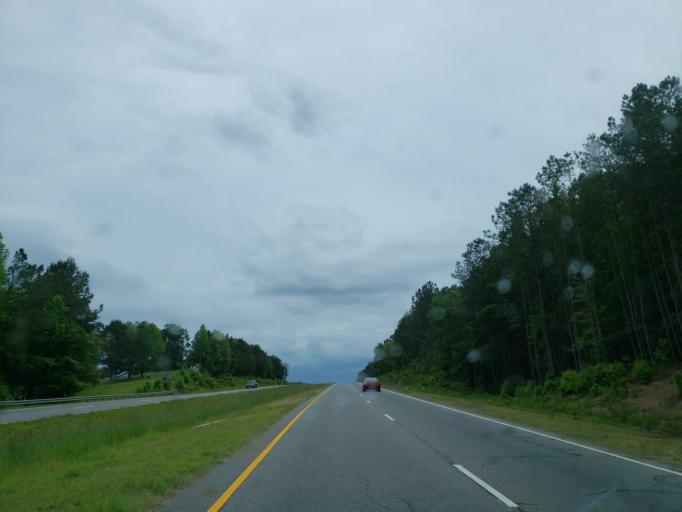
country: US
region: Georgia
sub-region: Haralson County
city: Bremen
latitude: 33.7491
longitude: -85.1604
